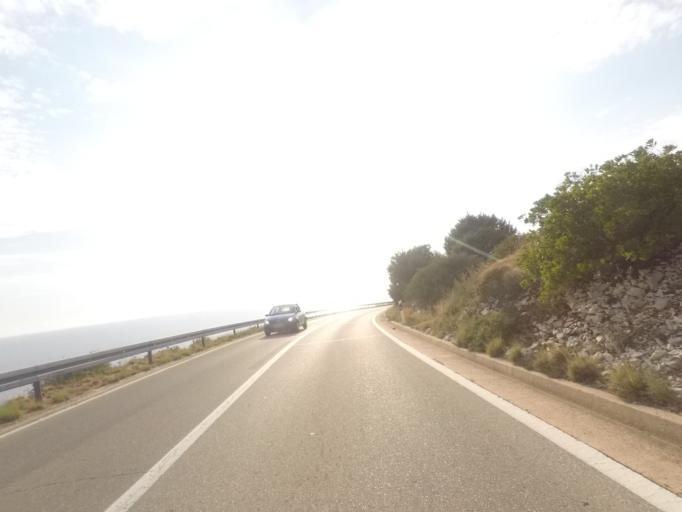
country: HR
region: Splitsko-Dalmatinska
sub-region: Grad Hvar
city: Hvar
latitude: 43.1578
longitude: 16.5048
